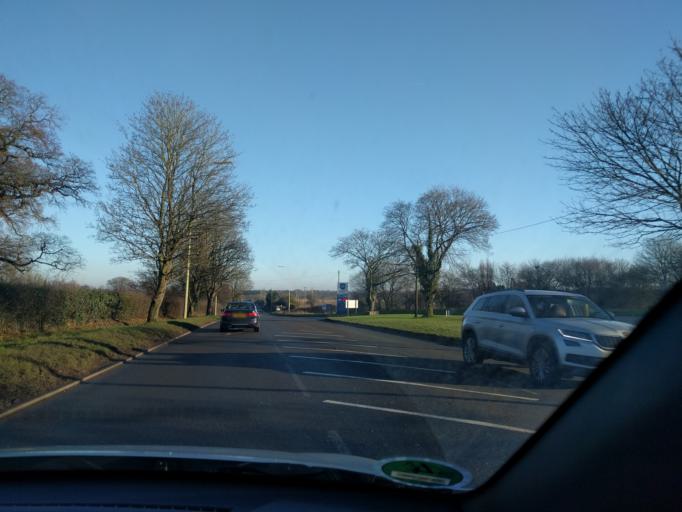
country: GB
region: England
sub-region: Staffordshire
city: Featherstone
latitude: 52.6537
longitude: -2.0773
